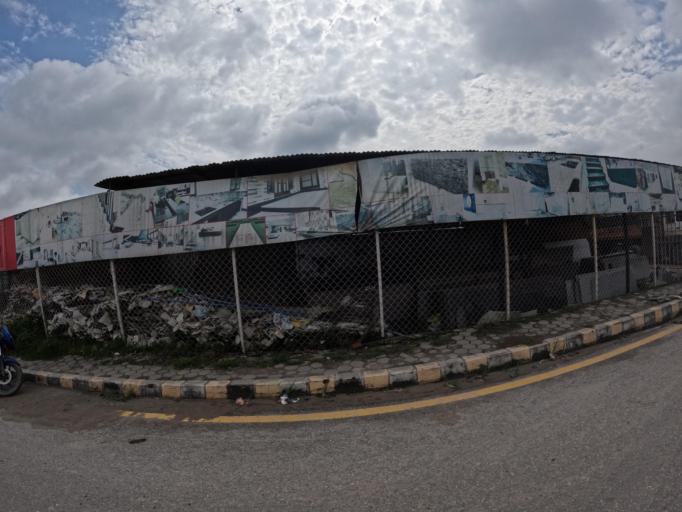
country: NP
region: Central Region
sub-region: Bagmati Zone
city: Kathmandu
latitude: 27.7595
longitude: 85.3163
